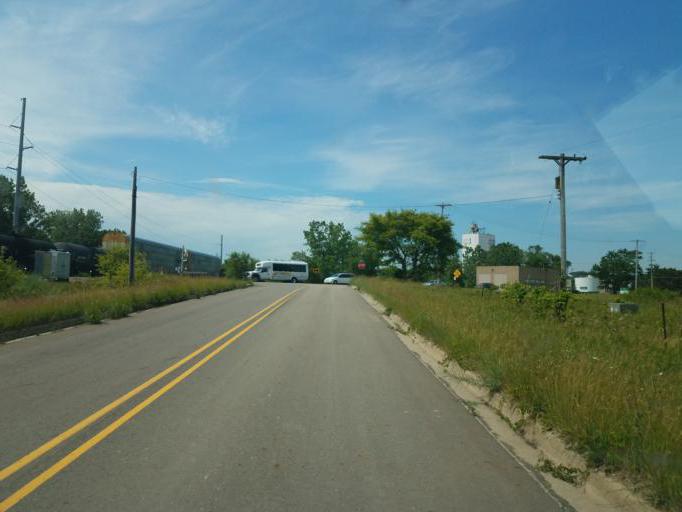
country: US
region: Michigan
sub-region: Eaton County
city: Charlotte
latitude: 42.5828
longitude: -84.8240
